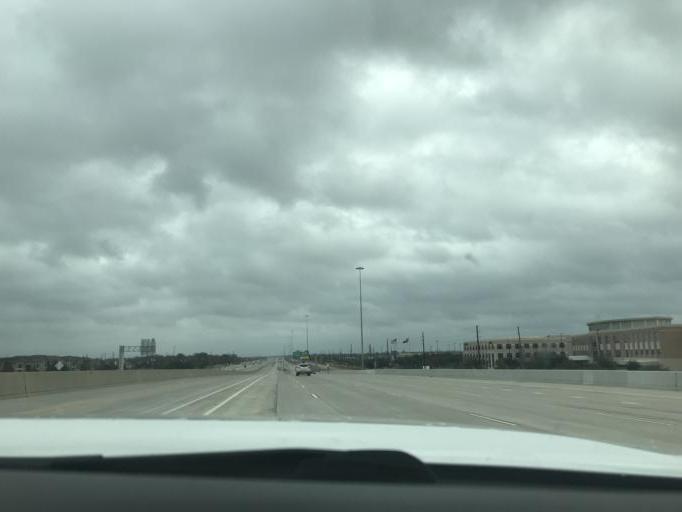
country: US
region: Texas
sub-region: Fort Bend County
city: Greatwood
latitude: 29.5560
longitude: -95.7162
